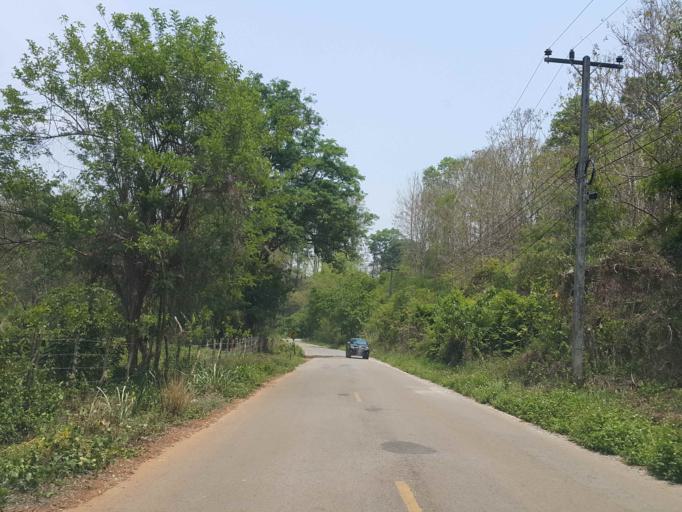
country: TH
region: Chiang Mai
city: Mae Taeng
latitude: 19.1963
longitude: 98.8540
